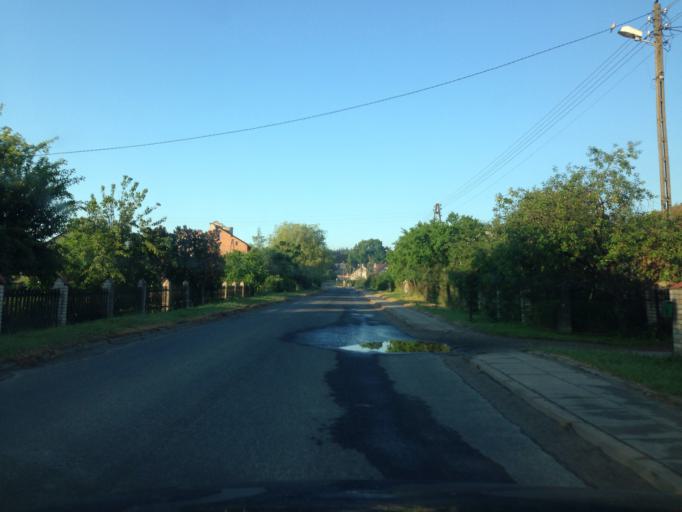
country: PL
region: Pomeranian Voivodeship
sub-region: Powiat tczewski
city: Gniew
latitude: 53.8027
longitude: 18.8125
